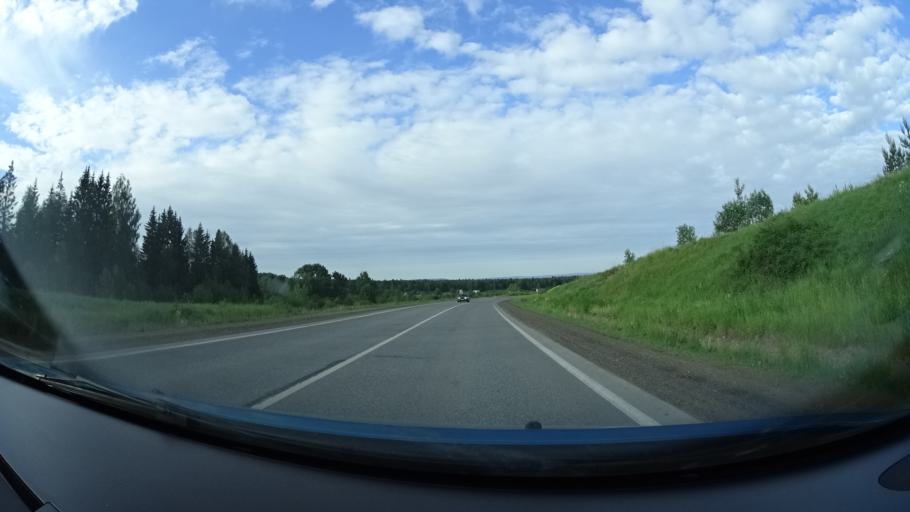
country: RU
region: Perm
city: Osa
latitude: 57.3989
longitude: 55.6234
